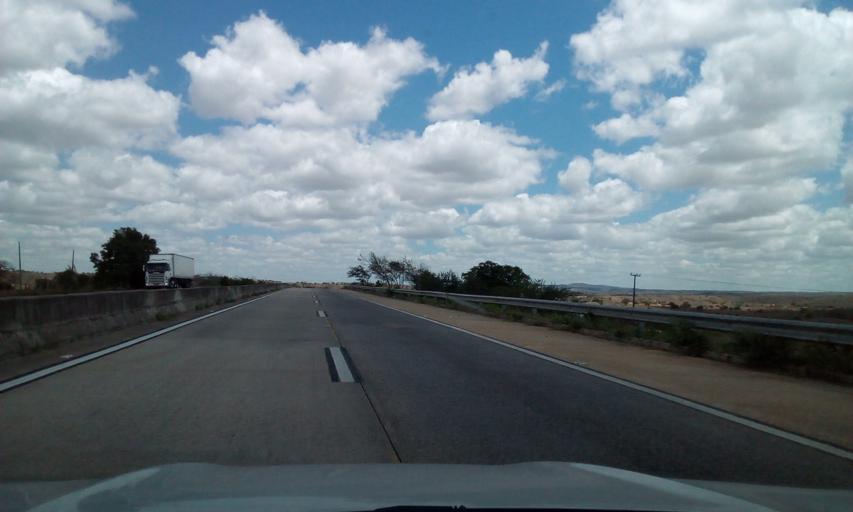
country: BR
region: Alagoas
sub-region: Porto Real Do Colegio
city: Porto Real do Colegio
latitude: -10.1351
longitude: -36.8010
